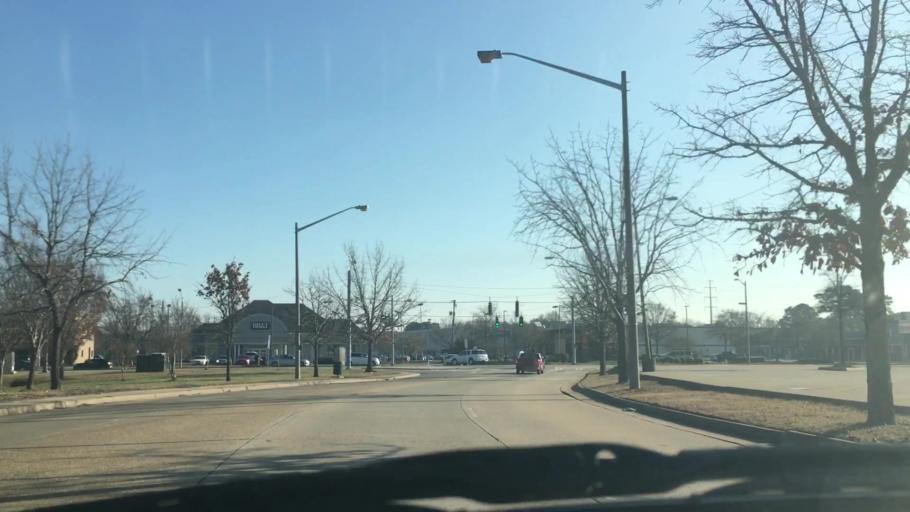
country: US
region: Virginia
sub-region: City of Norfolk
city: Norfolk
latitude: 36.9170
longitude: -76.2688
